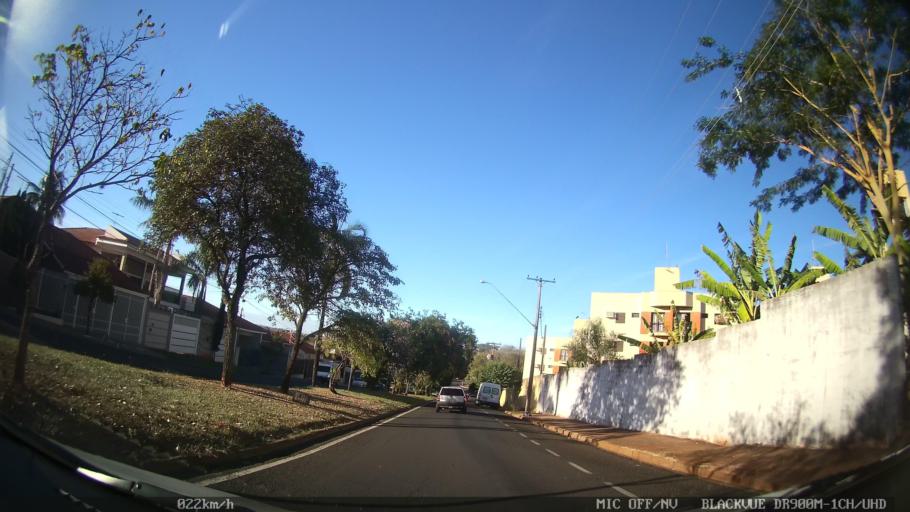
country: BR
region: Sao Paulo
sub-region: Sao Jose Do Rio Preto
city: Sao Jose do Rio Preto
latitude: -20.8297
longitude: -49.3672
